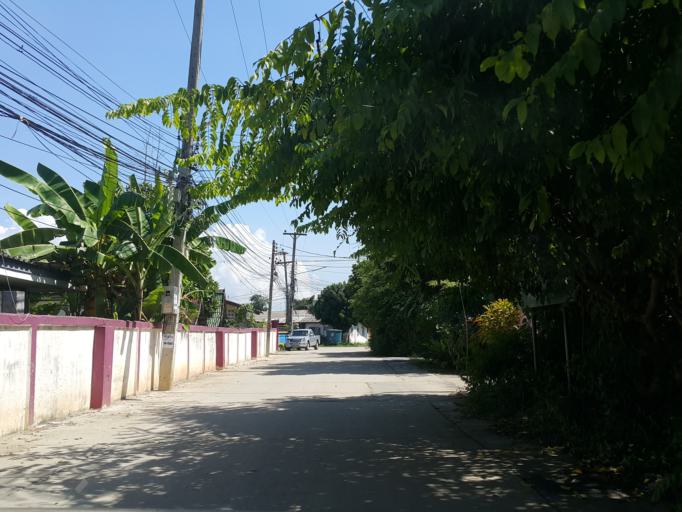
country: TH
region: Chiang Mai
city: Saraphi
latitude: 18.7629
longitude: 99.0553
